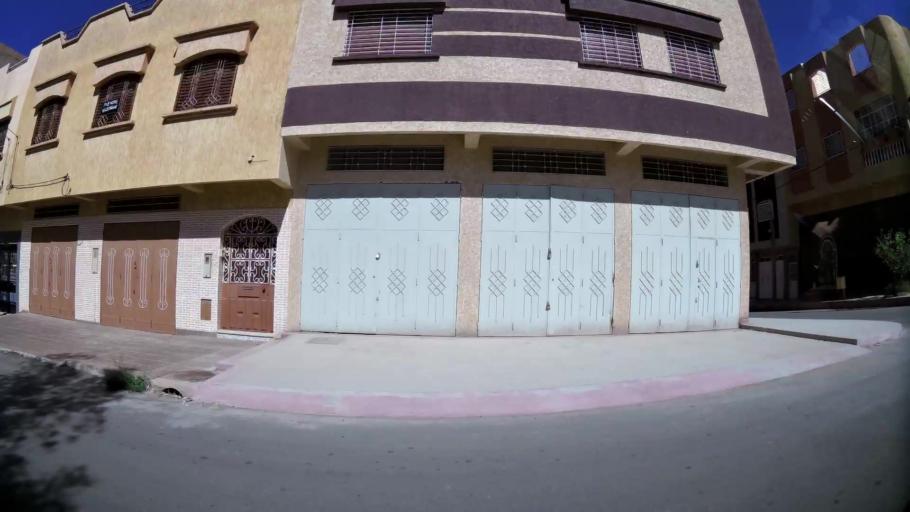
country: MA
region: Oriental
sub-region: Oujda-Angad
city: Oujda
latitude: 34.6593
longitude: -1.9167
